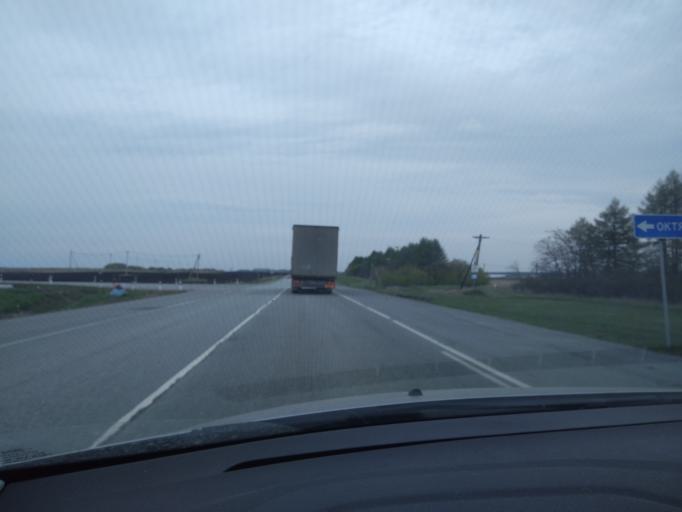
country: RU
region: Sverdlovsk
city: Yelanskiy
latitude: 56.7747
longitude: 62.4585
